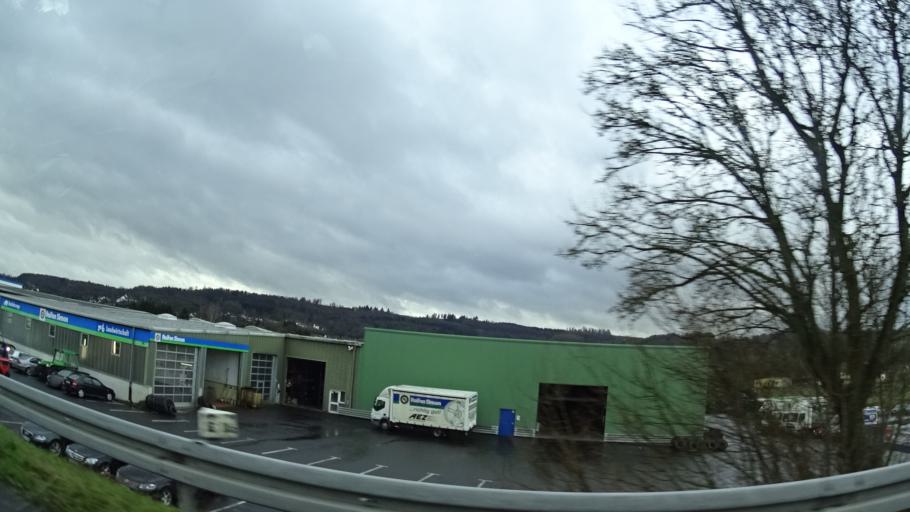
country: DE
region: Hesse
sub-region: Regierungsbezirk Darmstadt
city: Schluchtern
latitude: 50.3570
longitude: 9.5244
